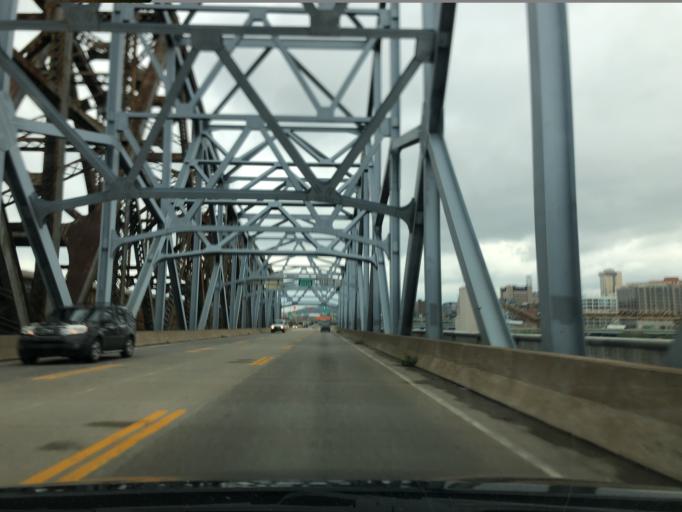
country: US
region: Kentucky
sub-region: Kenton County
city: Covington
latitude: 39.0917
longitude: -84.5194
